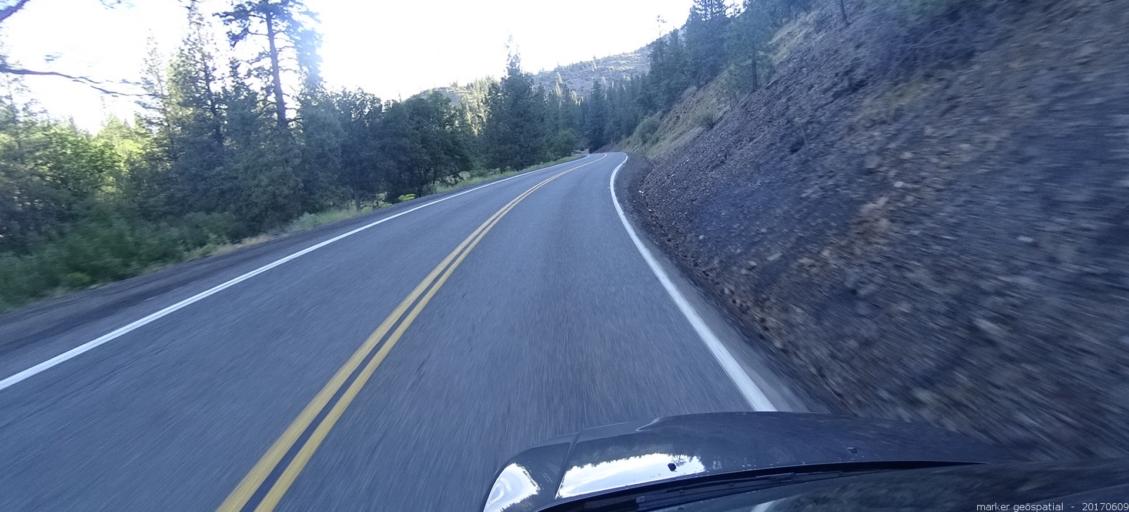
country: US
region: California
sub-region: Siskiyou County
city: Weed
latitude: 41.3339
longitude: -122.7511
